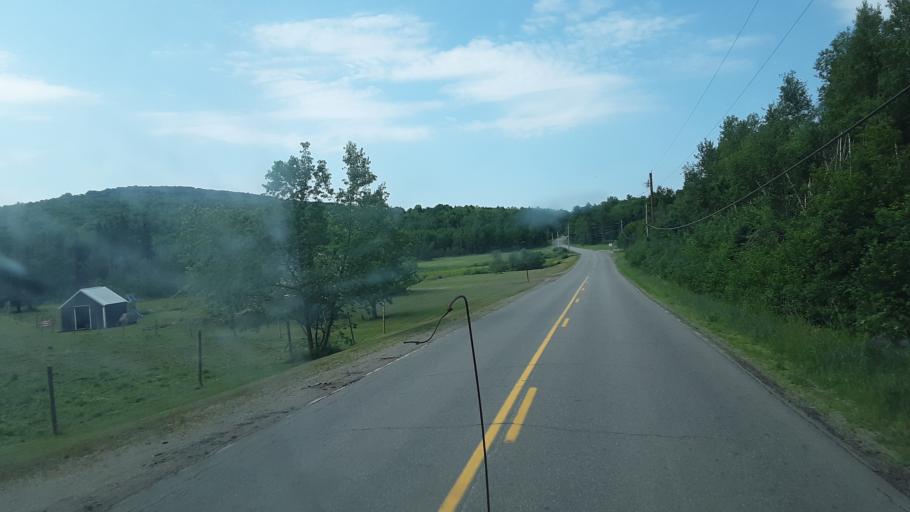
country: US
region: Maine
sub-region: Waldo County
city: Frankfort
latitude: 44.6014
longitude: -68.9394
